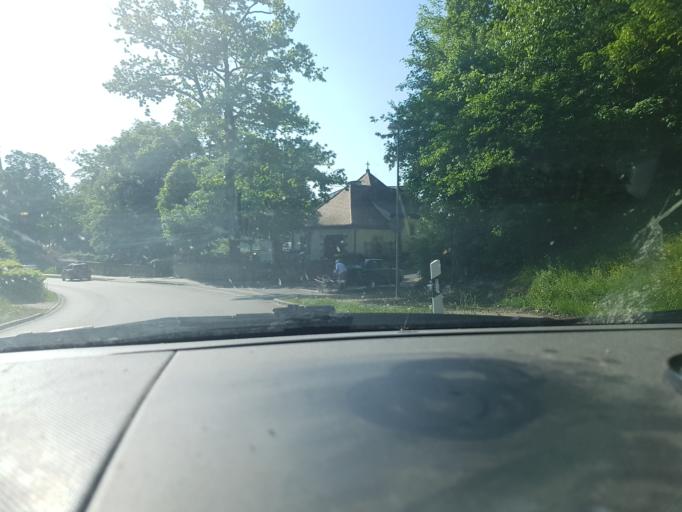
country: DE
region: Bavaria
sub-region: Regierungsbezirk Mittelfranken
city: Georgensgmund
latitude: 49.1882
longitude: 11.0096
